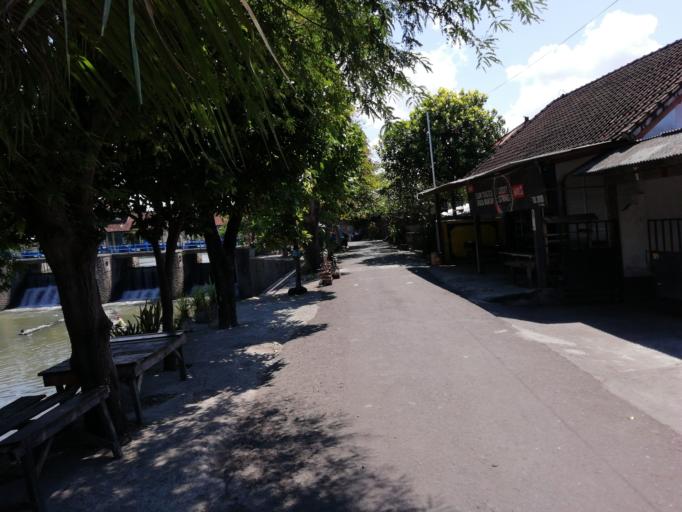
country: ID
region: Bali
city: Karyadharma
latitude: -8.6848
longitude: 115.1979
